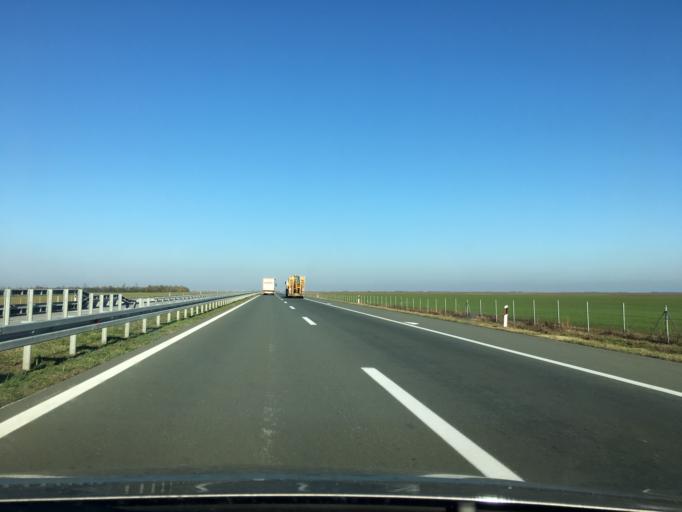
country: RS
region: Autonomna Pokrajina Vojvodina
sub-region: Severnobacki Okrug
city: Mali Igos
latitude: 45.6976
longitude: 19.7221
